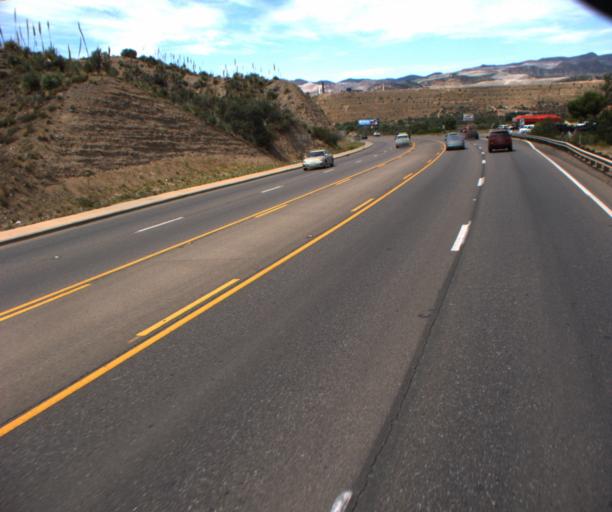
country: US
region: Arizona
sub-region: Gila County
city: Central Heights-Midland City
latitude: 33.4186
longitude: -110.8216
